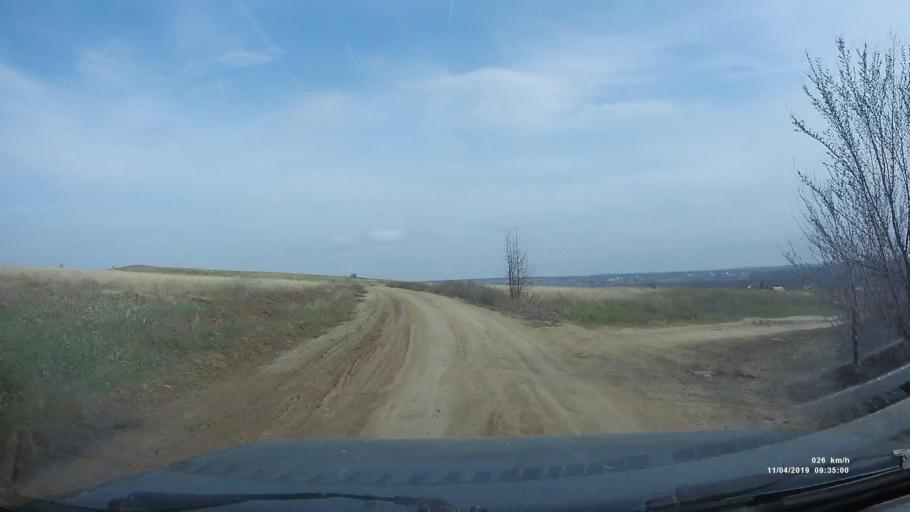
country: RU
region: Rostov
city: Staraya Stanitsa
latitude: 48.2707
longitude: 40.3716
